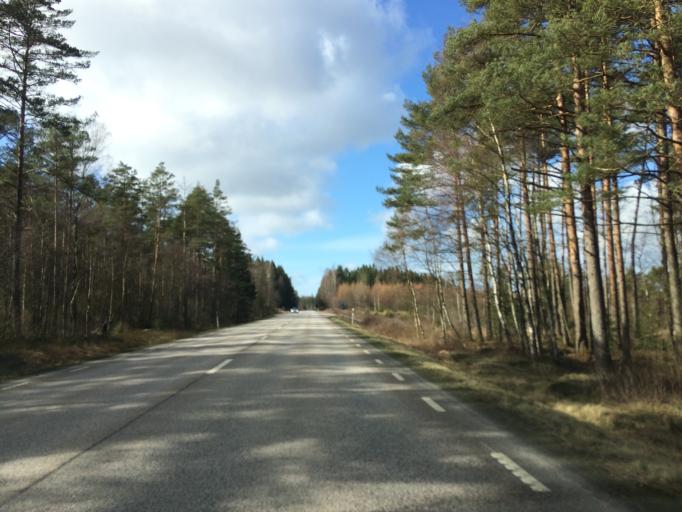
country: SE
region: Halland
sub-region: Laholms Kommun
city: Knared
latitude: 56.4923
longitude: 13.3979
